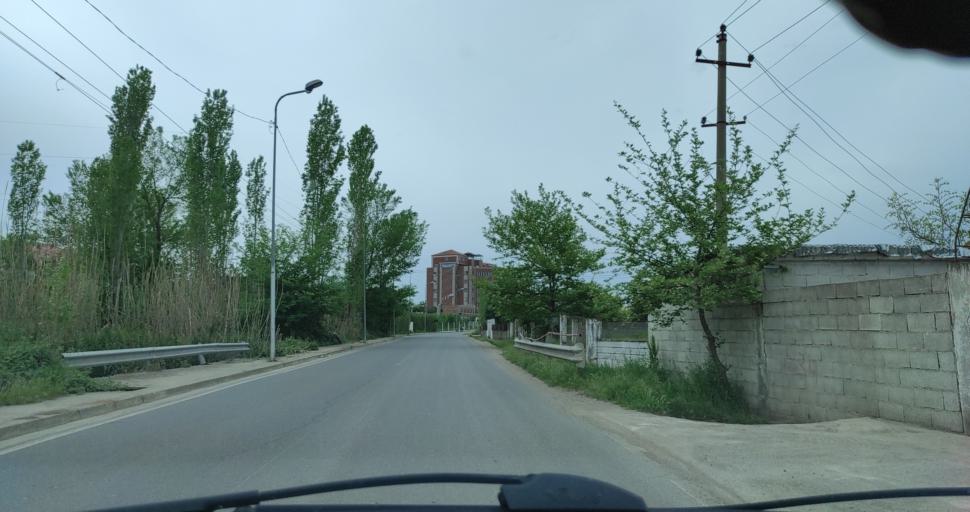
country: AL
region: Lezhe
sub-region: Rrethi i Kurbinit
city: Lac
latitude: 41.6194
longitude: 19.7106
